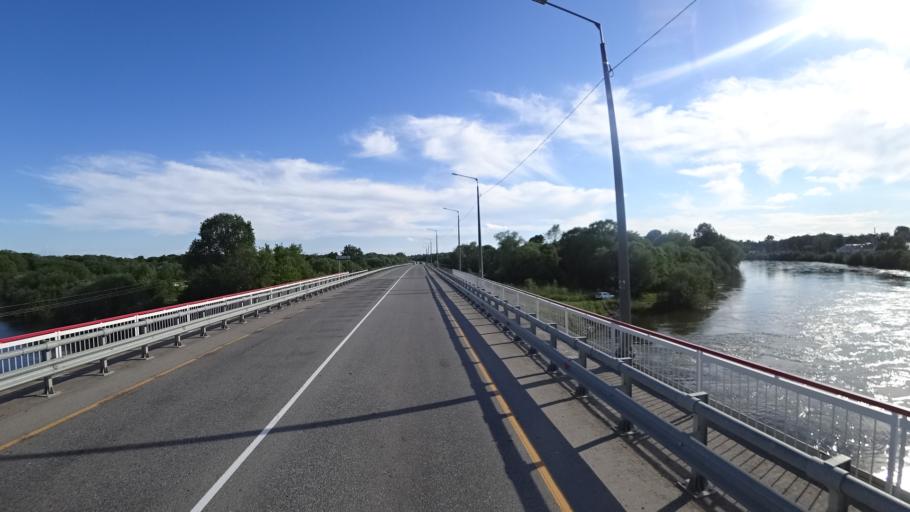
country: RU
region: Khabarovsk Krai
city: Khor
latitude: 47.8849
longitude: 134.9735
